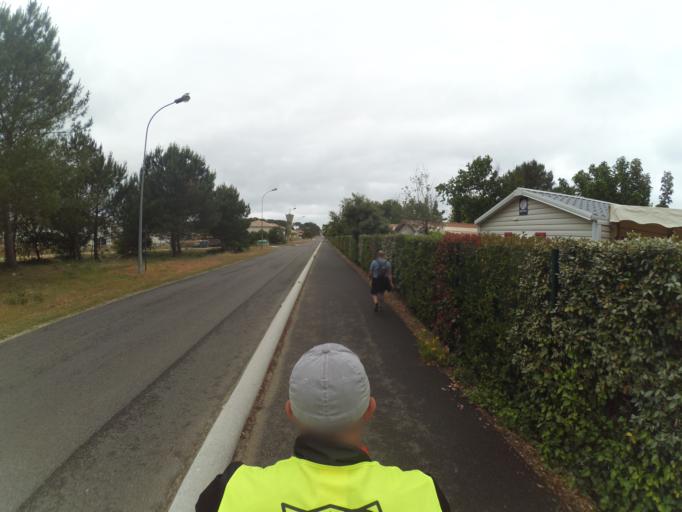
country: FR
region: Aquitaine
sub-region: Departement des Landes
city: Mimizan
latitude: 44.2168
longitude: -1.2832
